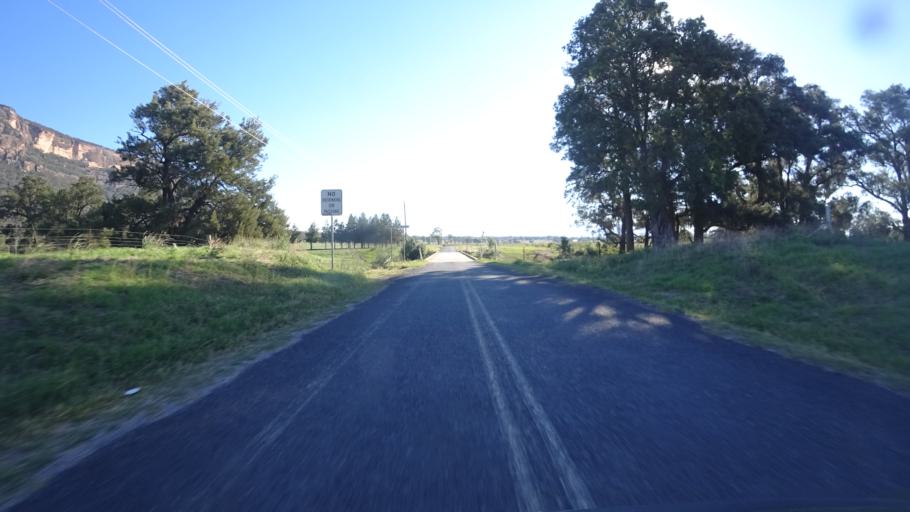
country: AU
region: New South Wales
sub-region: Mid-Western Regional
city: Kandos
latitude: -33.1001
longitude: 150.2316
